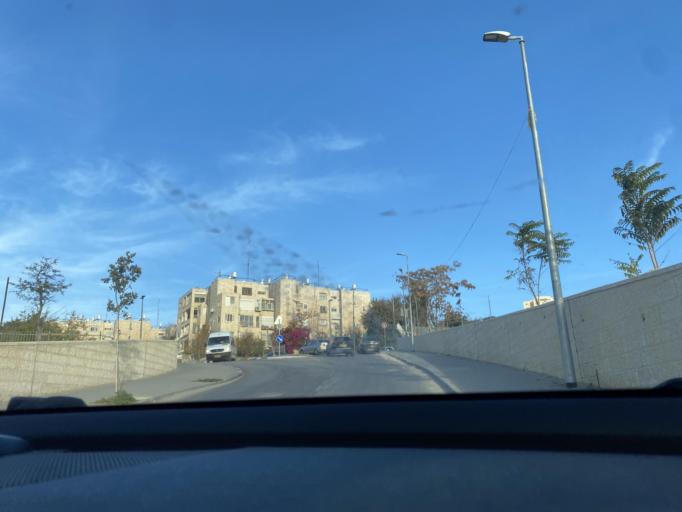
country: PS
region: West Bank
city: Ash Shaykh Sa`d
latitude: 31.7434
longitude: 35.2398
